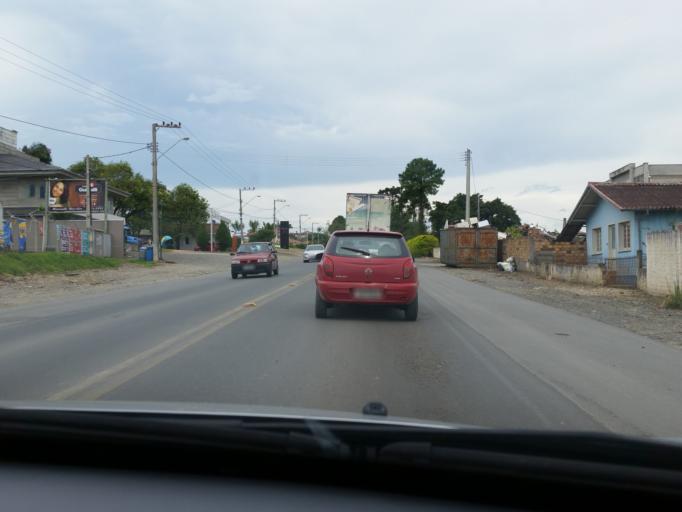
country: BR
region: Santa Catarina
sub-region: Rio Do Sul
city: Rio do Sul
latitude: -27.2582
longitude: -49.9288
